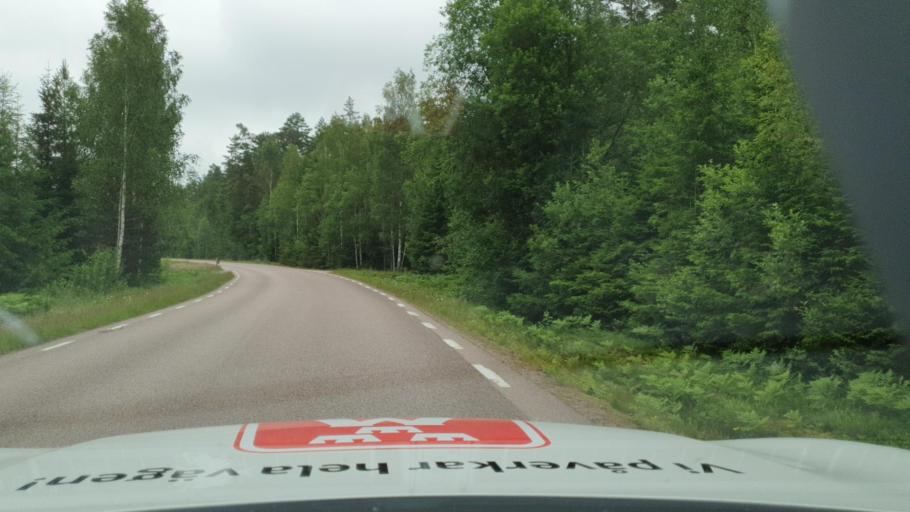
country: SE
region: Vaermland
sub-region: Kristinehamns Kommun
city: Kristinehamn
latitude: 59.4942
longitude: 13.9562
